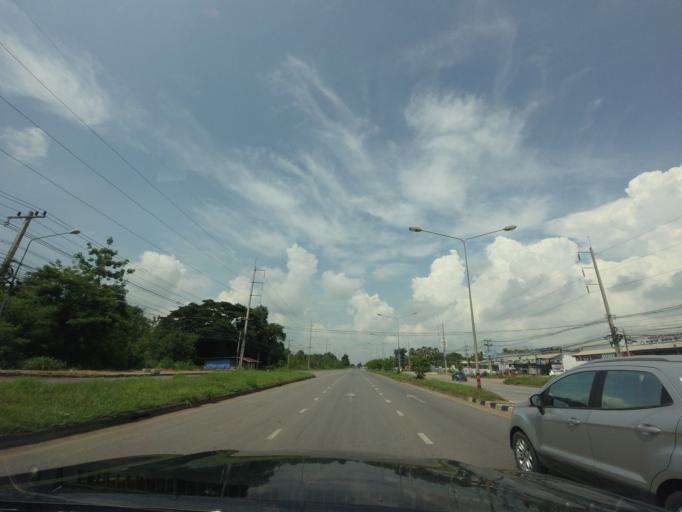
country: TH
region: Khon Kaen
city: Ban Fang
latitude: 16.4499
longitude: 102.7139
